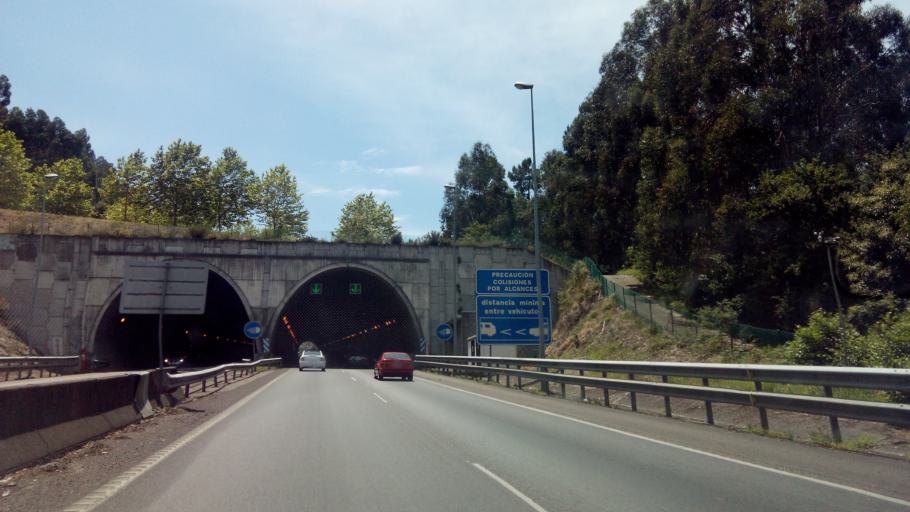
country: ES
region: Galicia
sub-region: Provincia de Pontevedra
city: Vigo
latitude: 42.2545
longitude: -8.6770
